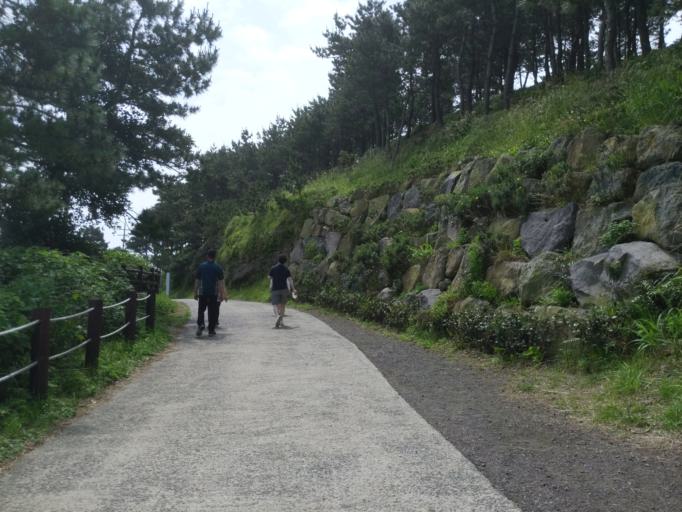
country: KR
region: Jeju-do
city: Gaigeturi
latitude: 33.2029
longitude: 126.2915
